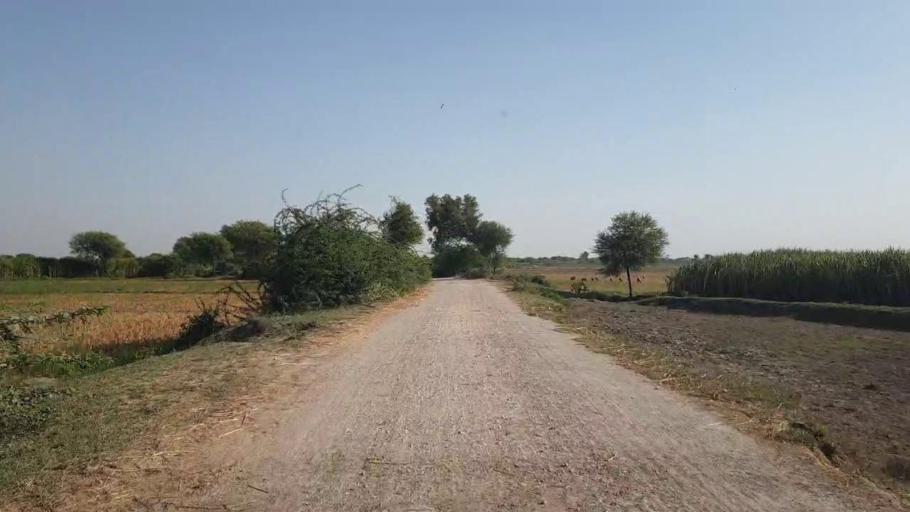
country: PK
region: Sindh
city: Matli
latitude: 25.0227
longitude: 68.7357
